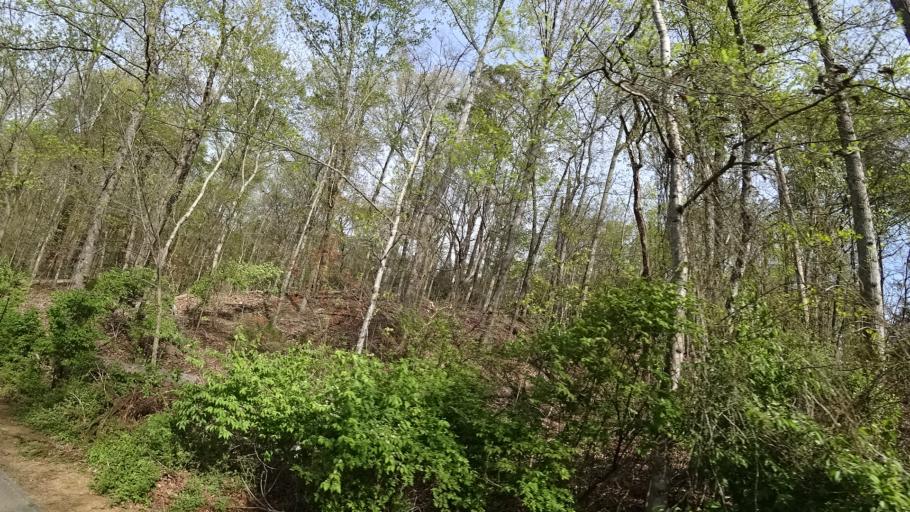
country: US
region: Tennessee
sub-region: Knox County
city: Knoxville
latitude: 35.9014
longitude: -83.9749
